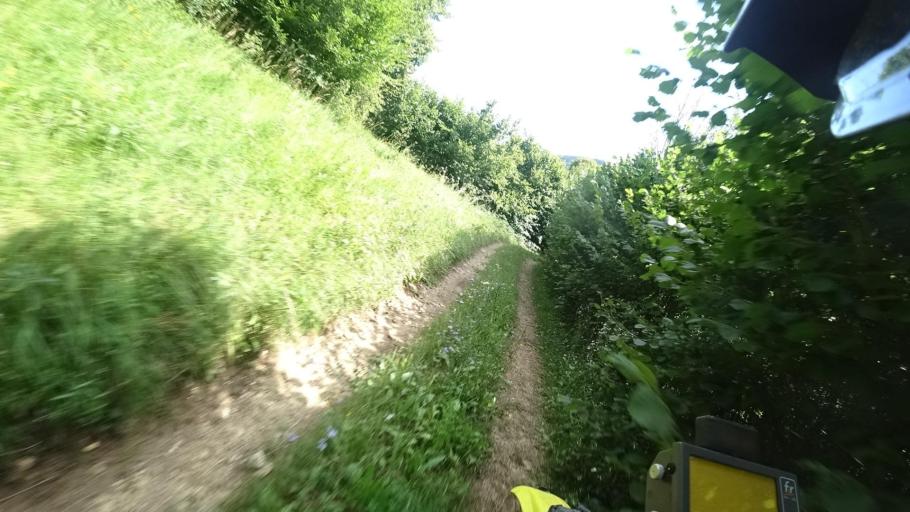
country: HR
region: Licko-Senjska
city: Brinje
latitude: 45.1082
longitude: 15.1092
